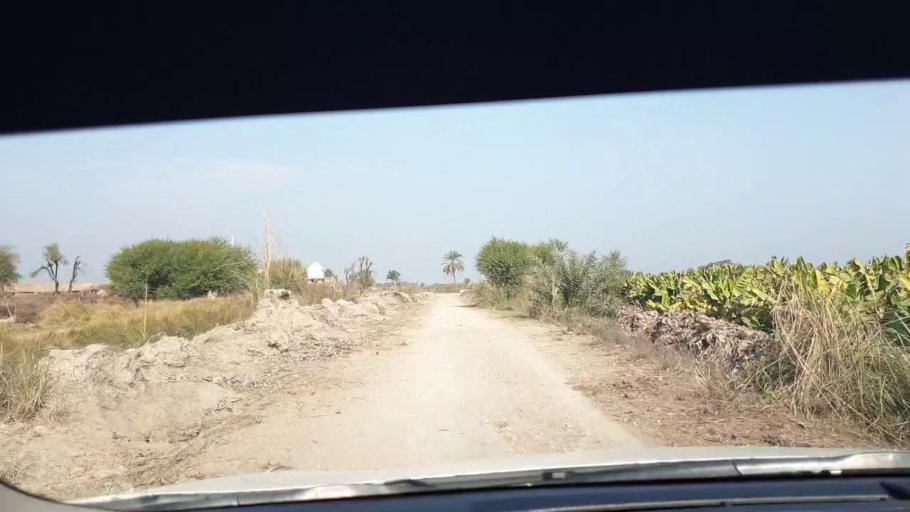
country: PK
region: Sindh
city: Tando Adam
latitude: 25.7392
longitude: 68.7026
